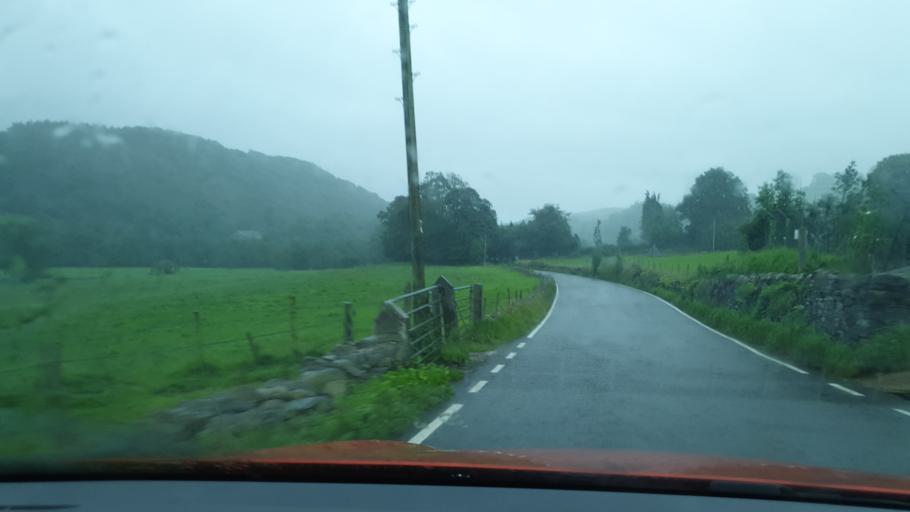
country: GB
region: England
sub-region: Cumbria
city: Ulverston
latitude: 54.2489
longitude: -3.0682
